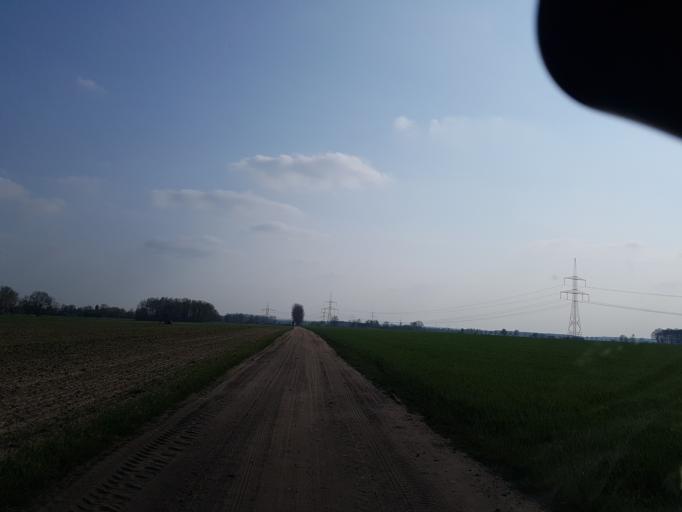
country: DE
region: Brandenburg
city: Doberlug-Kirchhain
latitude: 51.6015
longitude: 13.5338
